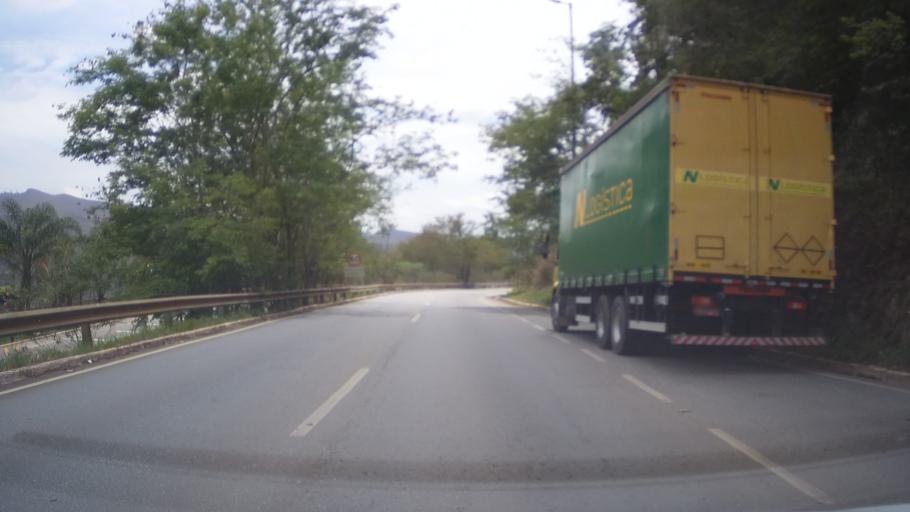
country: BR
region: Minas Gerais
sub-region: Nova Lima
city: Nova Lima
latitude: -19.9976
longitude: -43.8825
